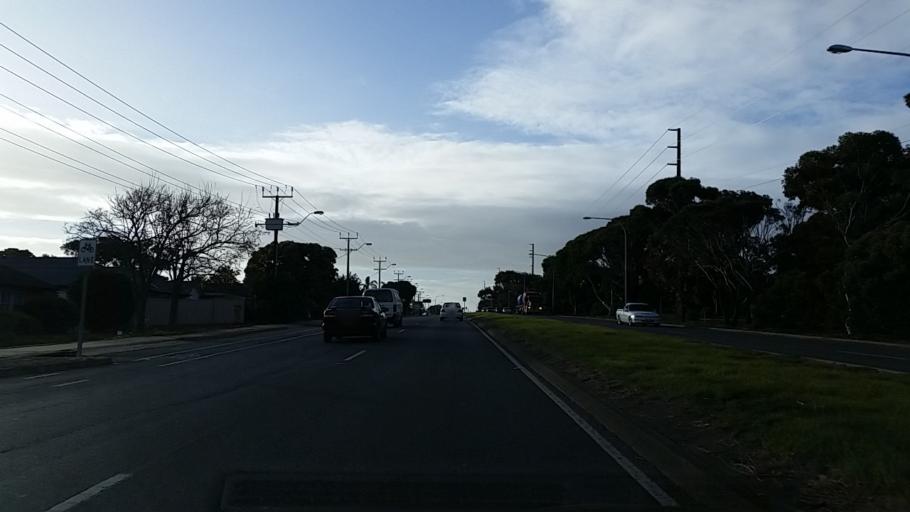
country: AU
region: South Australia
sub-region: Adelaide
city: Port Noarlunga
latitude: -35.1342
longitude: 138.4859
